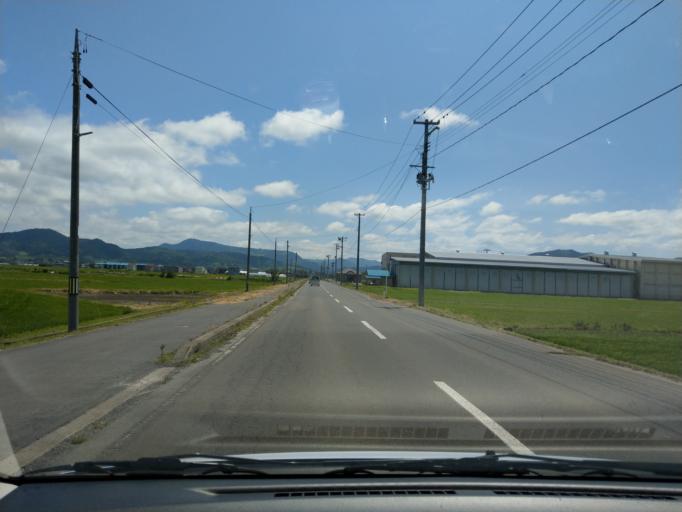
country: JP
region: Aomori
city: Kuroishi
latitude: 40.5814
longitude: 140.5509
